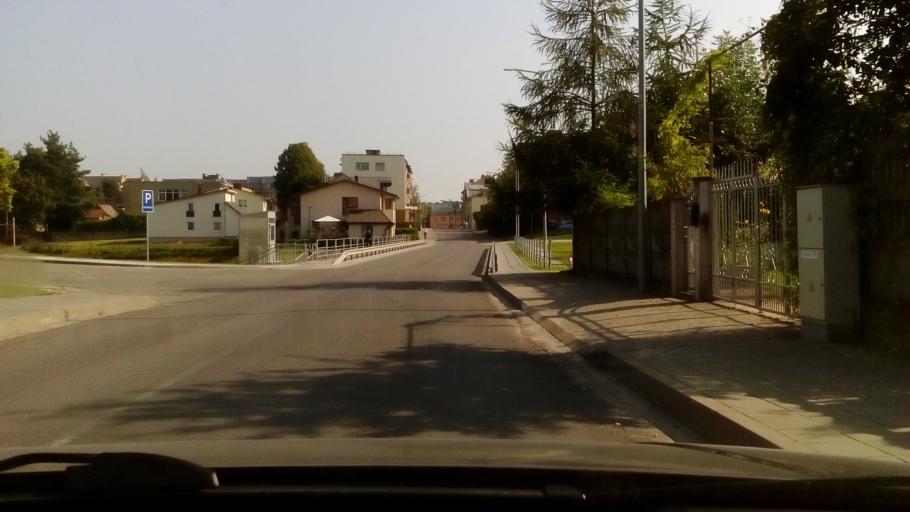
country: LT
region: Alytaus apskritis
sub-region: Alytus
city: Alytus
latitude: 54.3981
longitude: 24.0410
